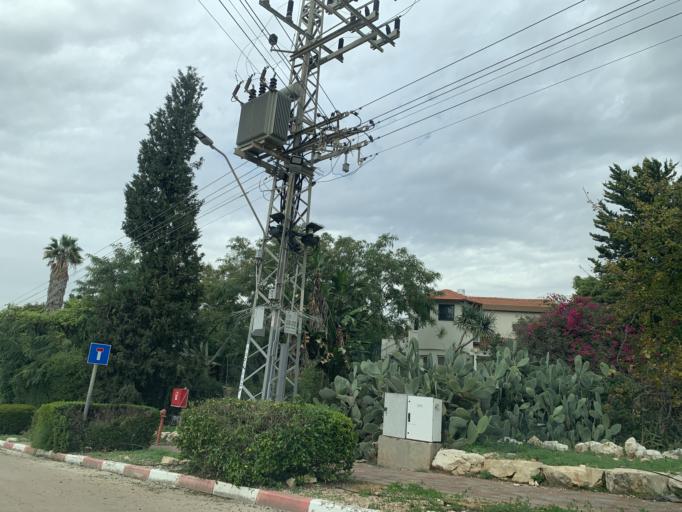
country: IL
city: Nirit
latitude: 32.1464
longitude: 34.9836
